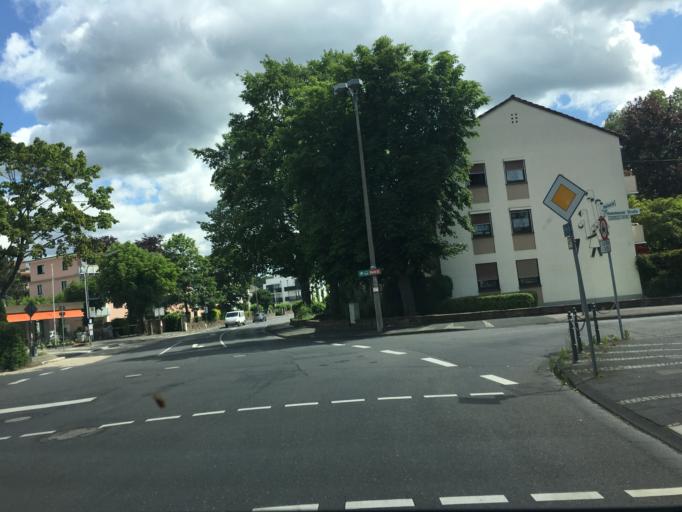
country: DE
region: Rheinland-Pfalz
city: Bad Neuenahr-Ahrweiler
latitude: 50.5452
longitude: 7.1302
